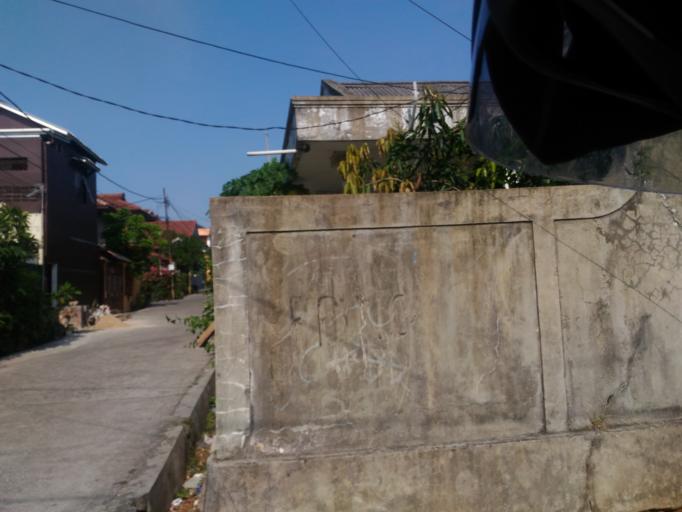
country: ID
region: West Java
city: Depok
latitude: -6.3472
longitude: 106.8397
